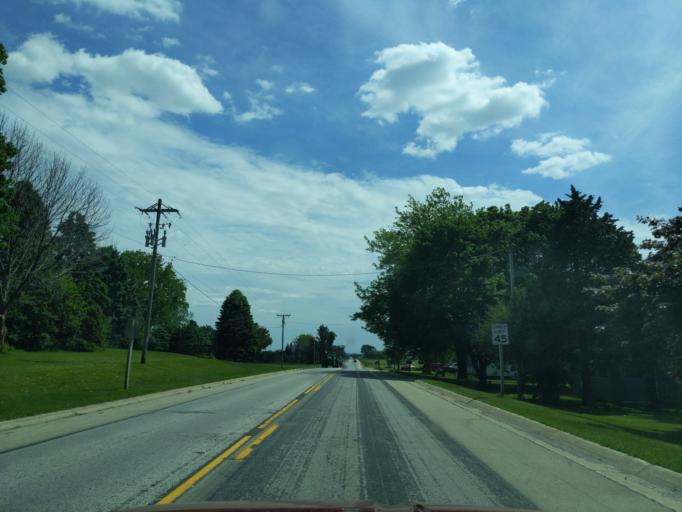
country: US
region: Wisconsin
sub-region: Dane County
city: De Forest
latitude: 43.3093
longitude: -89.3253
